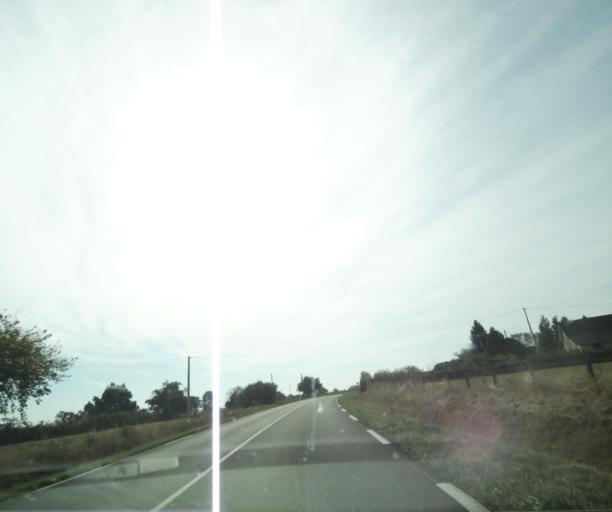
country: FR
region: Auvergne
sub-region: Departement de l'Allier
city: Saint-Francois
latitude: 46.4315
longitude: 3.9090
